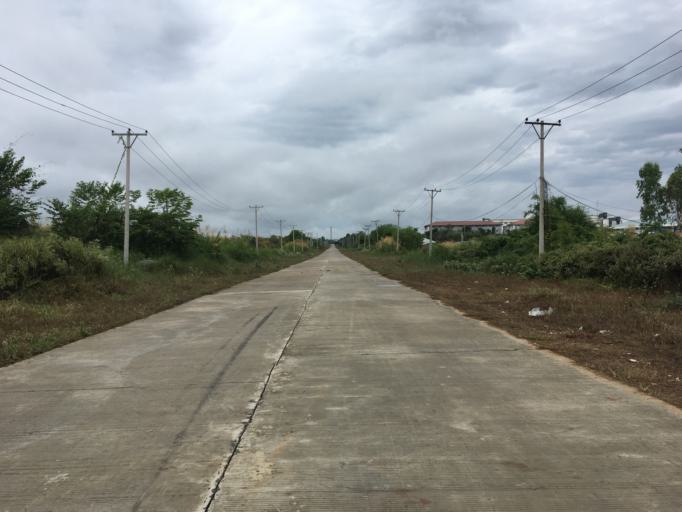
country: MM
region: Mandalay
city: Nay Pyi Taw
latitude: 19.6971
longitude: 96.1205
